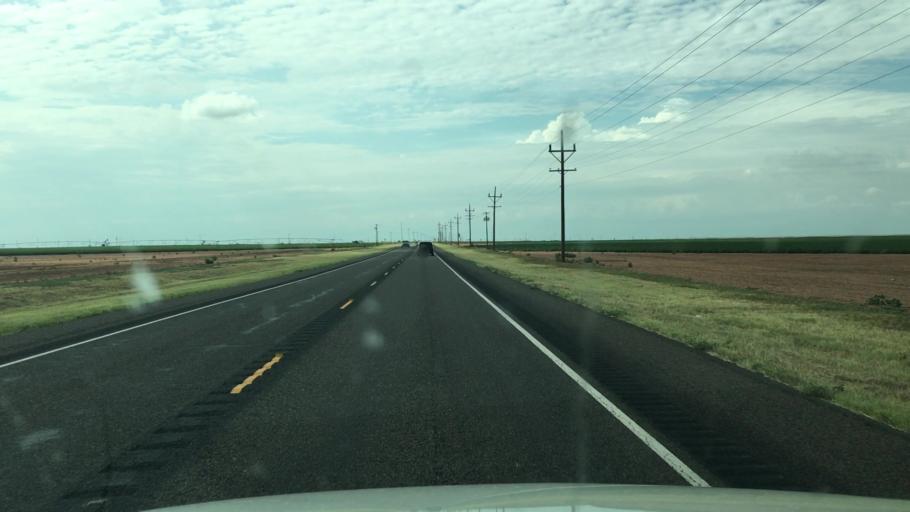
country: US
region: Texas
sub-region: Dawson County
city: Lamesa
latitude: 32.8846
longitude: -102.0843
